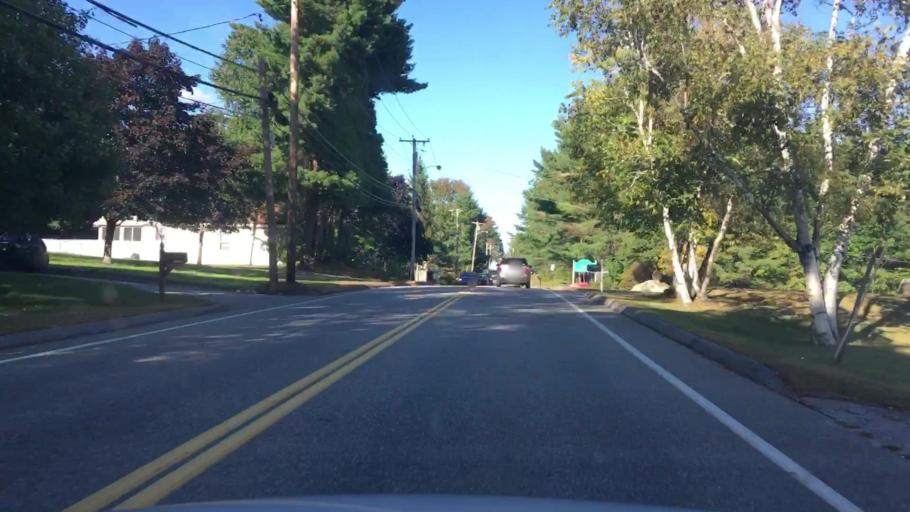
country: US
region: Maine
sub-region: Androscoggin County
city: Lewiston
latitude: 44.0842
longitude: -70.1689
